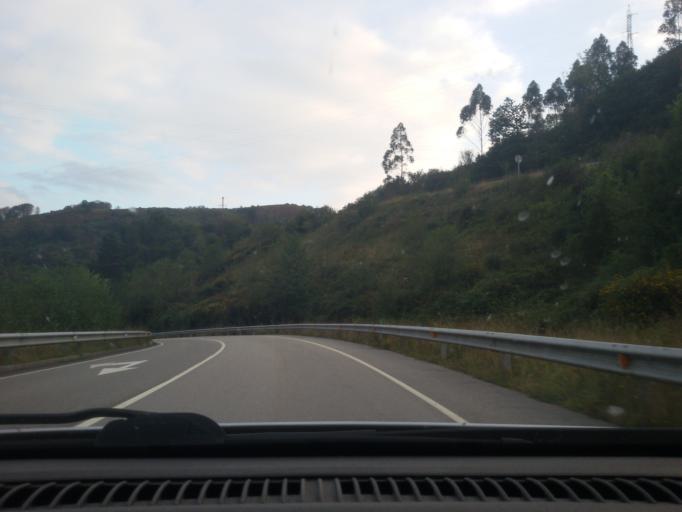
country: ES
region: Asturias
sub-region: Province of Asturias
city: Bimenes
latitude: 43.3413
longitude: -5.5796
